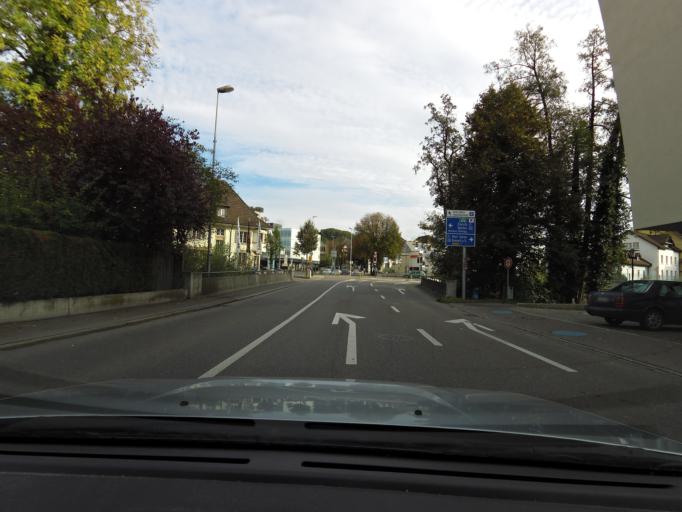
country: CH
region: Aargau
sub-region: Bezirk Lenzburg
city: Lenzburg
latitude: 47.3889
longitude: 8.1760
